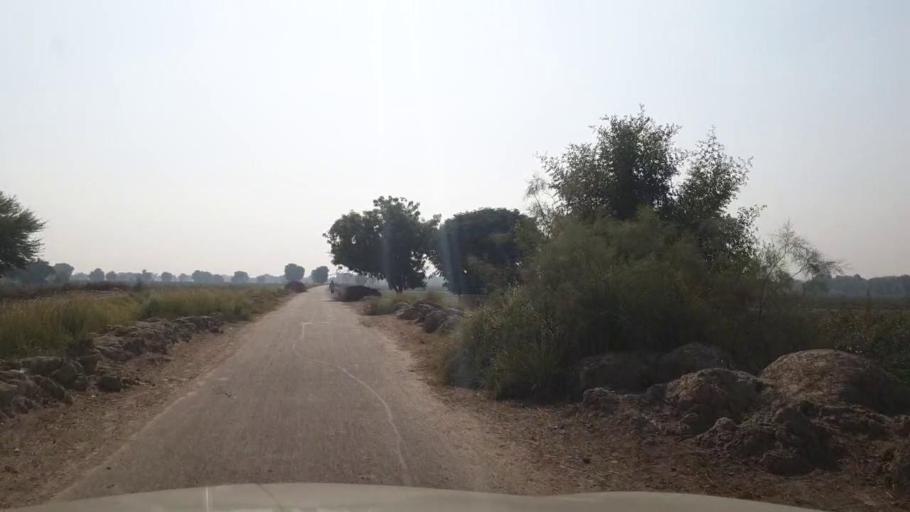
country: PK
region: Sindh
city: Bhan
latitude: 26.5250
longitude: 67.7793
